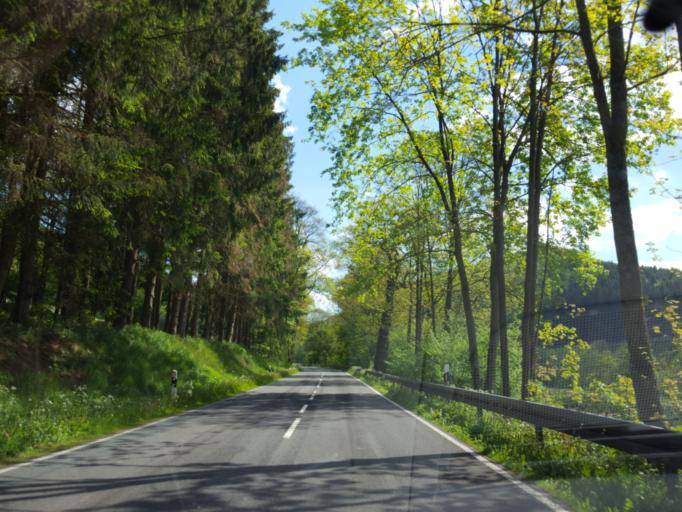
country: DE
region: North Rhine-Westphalia
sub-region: Regierungsbezirk Arnsberg
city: Olsberg
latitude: 51.3282
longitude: 8.4488
